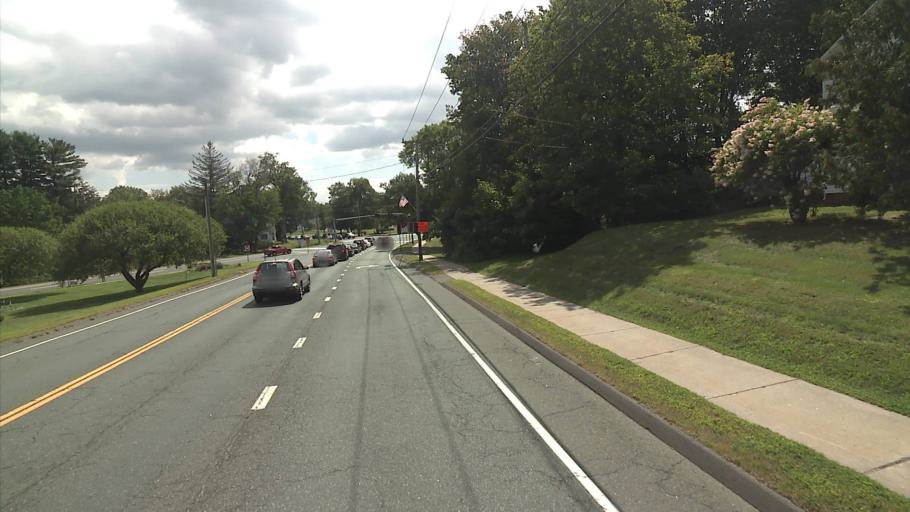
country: US
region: Connecticut
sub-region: Hartford County
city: Salmon Brook
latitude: 41.9547
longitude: -72.7908
